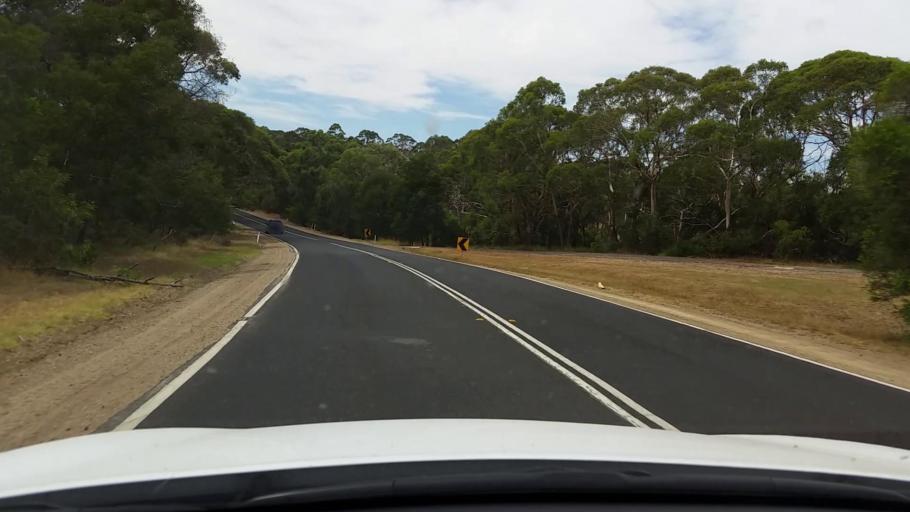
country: AU
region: Victoria
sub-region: Mornington Peninsula
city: Safety Beach
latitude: -38.3056
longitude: 145.0390
